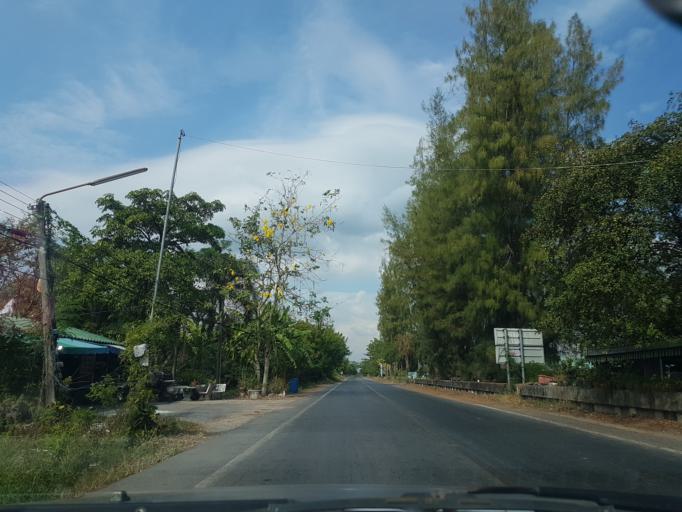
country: TH
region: Pathum Thani
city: Nong Suea
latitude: 14.1357
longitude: 100.8915
